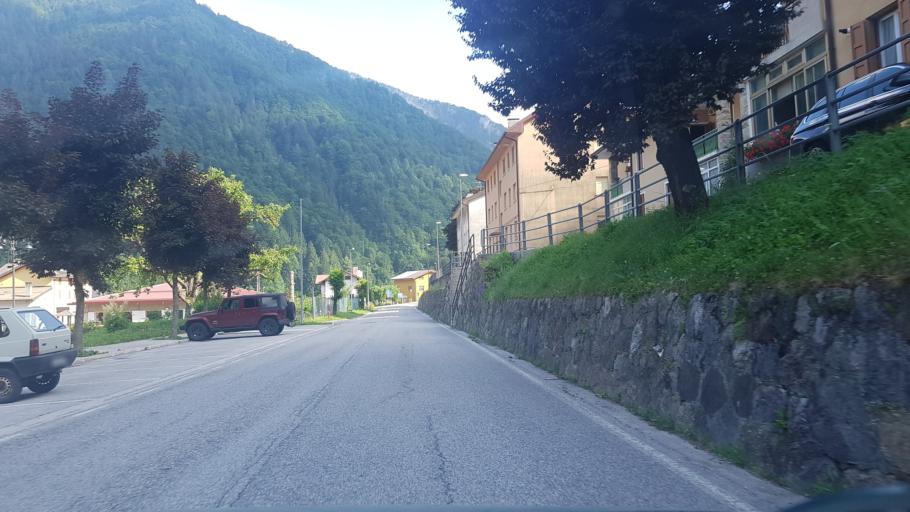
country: IT
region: Friuli Venezia Giulia
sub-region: Provincia di Udine
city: Pontebba
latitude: 46.5067
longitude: 13.3022
